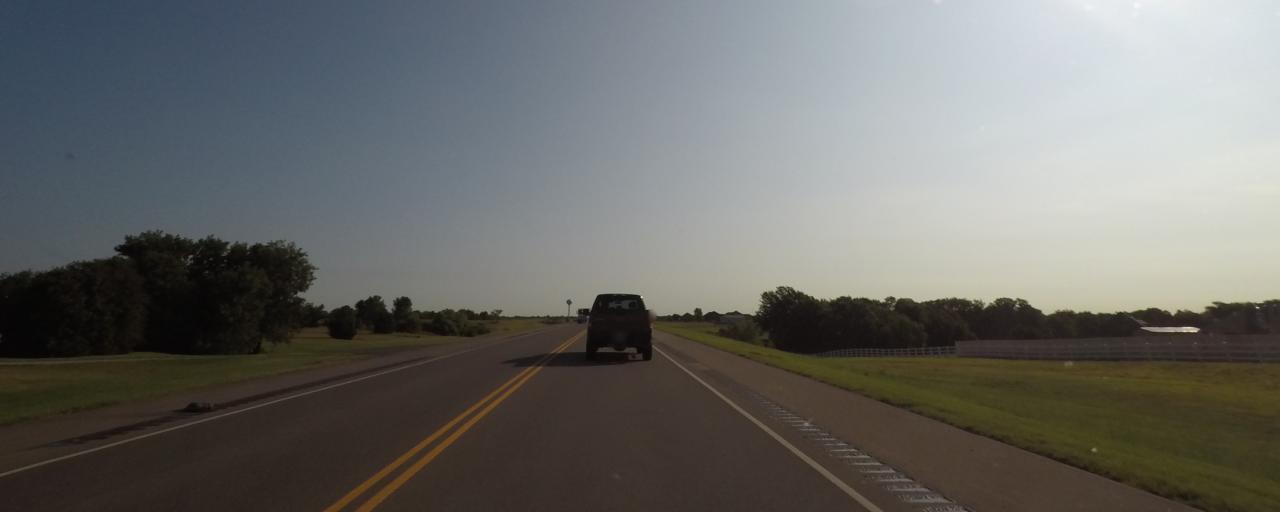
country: US
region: Oklahoma
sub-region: McClain County
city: Blanchard
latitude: 35.1135
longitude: -97.7128
